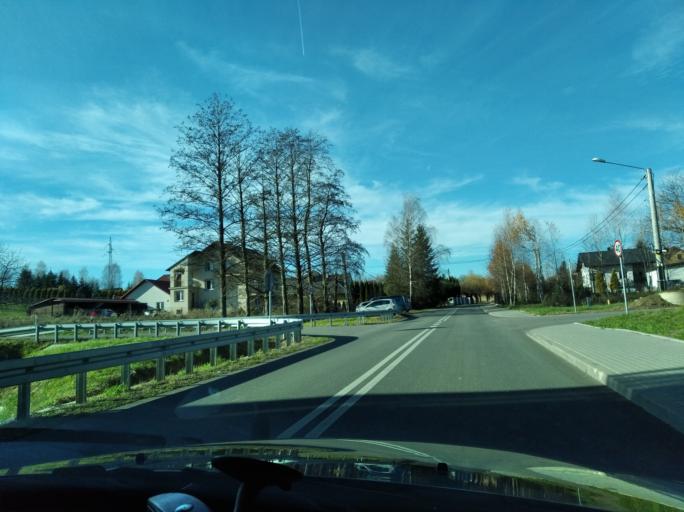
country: PL
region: Subcarpathian Voivodeship
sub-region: Powiat rzeszowski
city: Kielanowka
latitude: 50.0111
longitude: 21.9210
